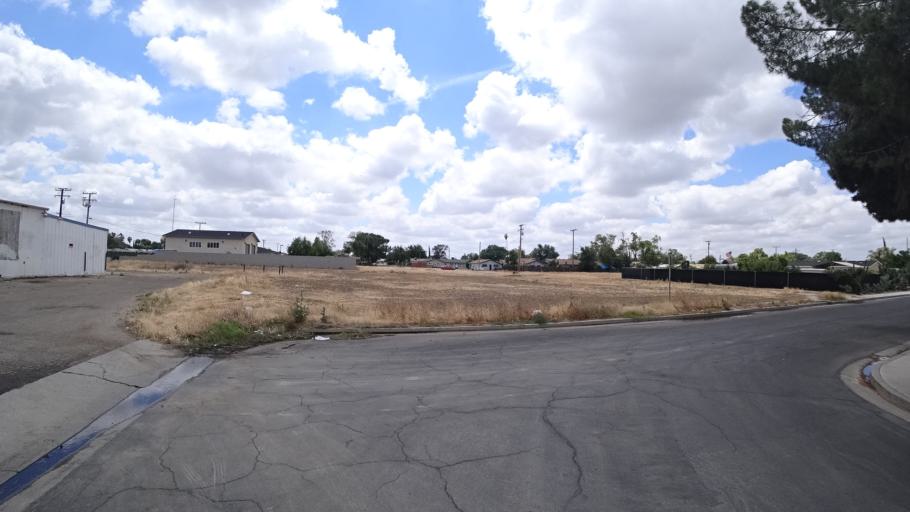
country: US
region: California
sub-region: Kings County
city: Hanford
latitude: 36.3134
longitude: -119.6737
